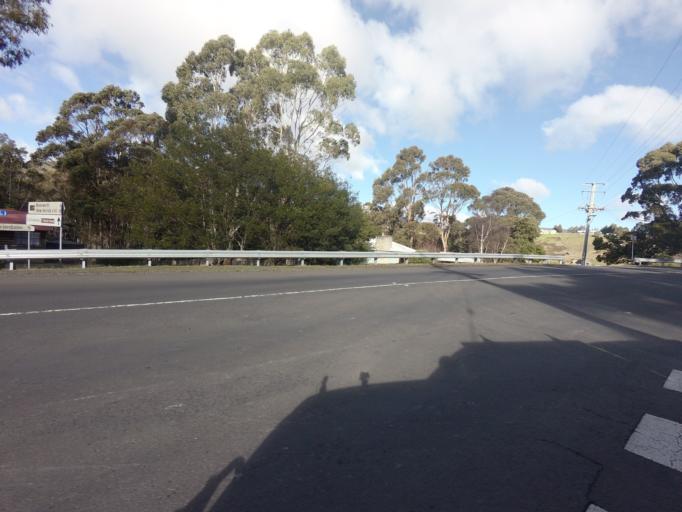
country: AU
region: Tasmania
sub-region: Glenorchy
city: Berriedale
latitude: -42.8243
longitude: 147.2036
